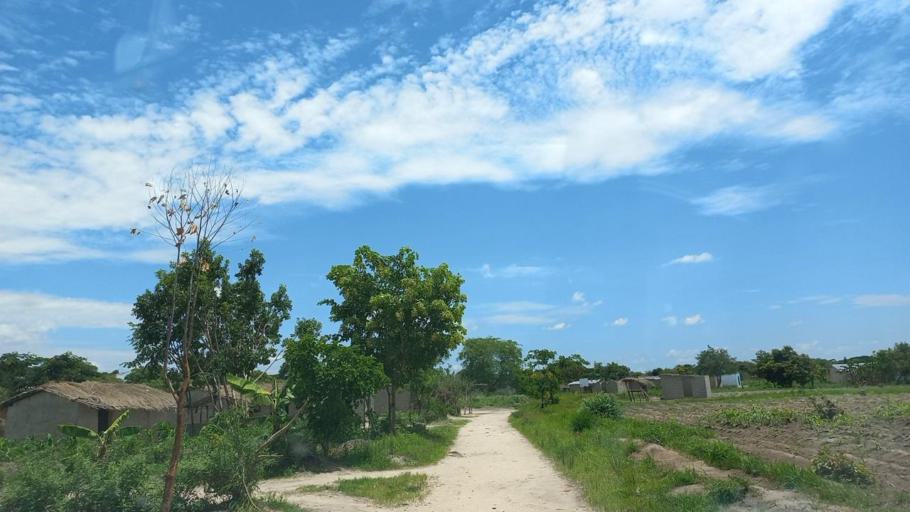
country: ZM
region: Copperbelt
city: Ndola
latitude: -12.8692
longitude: 28.4421
